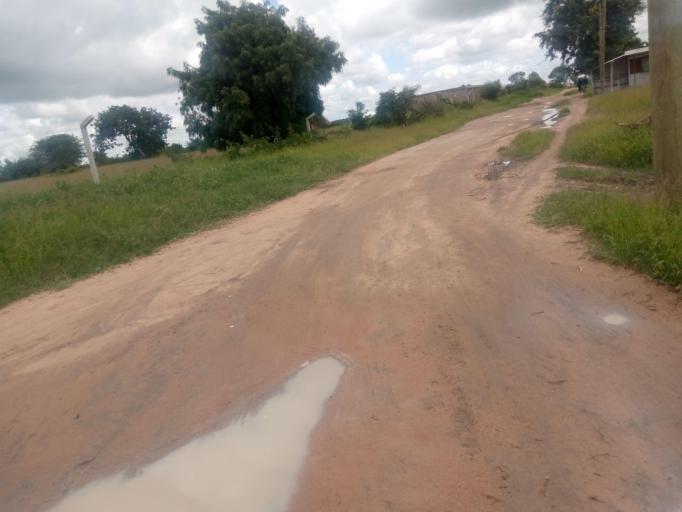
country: TZ
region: Dodoma
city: Dodoma
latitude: -6.1206
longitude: 35.7397
